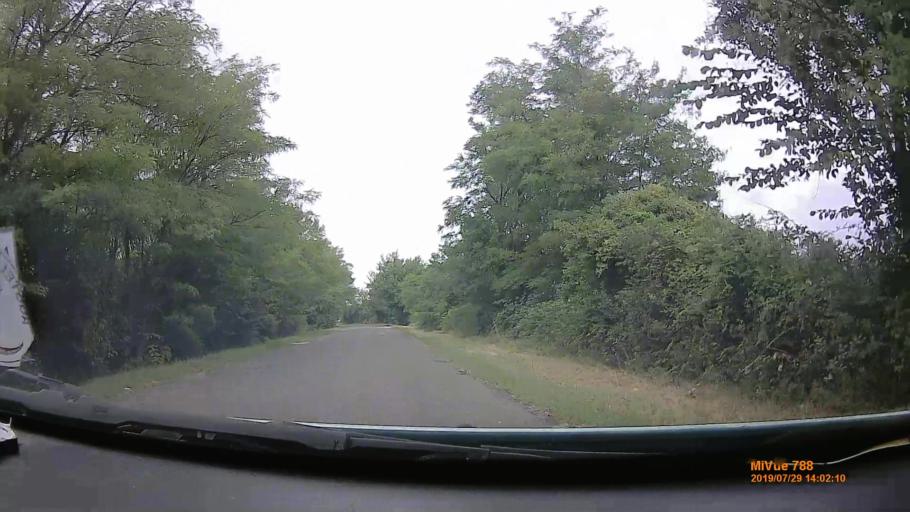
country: HU
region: Somogy
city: Balatonfoldvar
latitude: 46.8024
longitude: 17.9341
